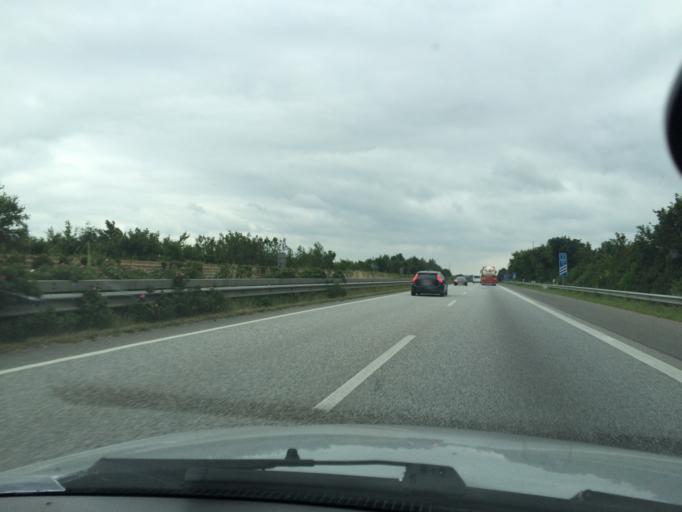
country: DE
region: Schleswig-Holstein
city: Jarplund-Weding
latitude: 54.7411
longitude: 9.3826
